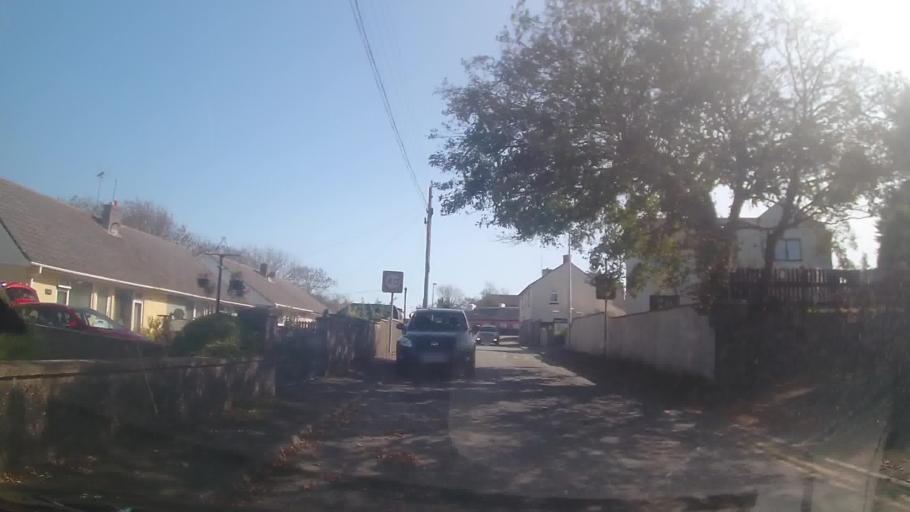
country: GB
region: Wales
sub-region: Pembrokeshire
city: Llanrhian
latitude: 51.9289
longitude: -5.1603
